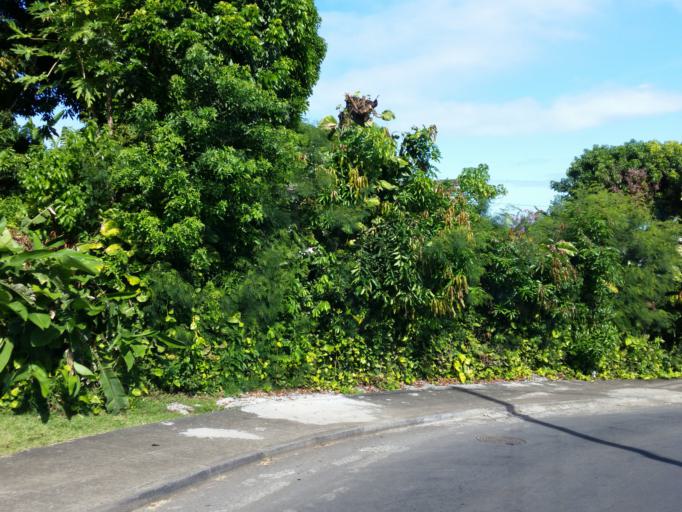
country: RE
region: Reunion
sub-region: Reunion
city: Sainte-Marie
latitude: -20.9169
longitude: 55.5329
